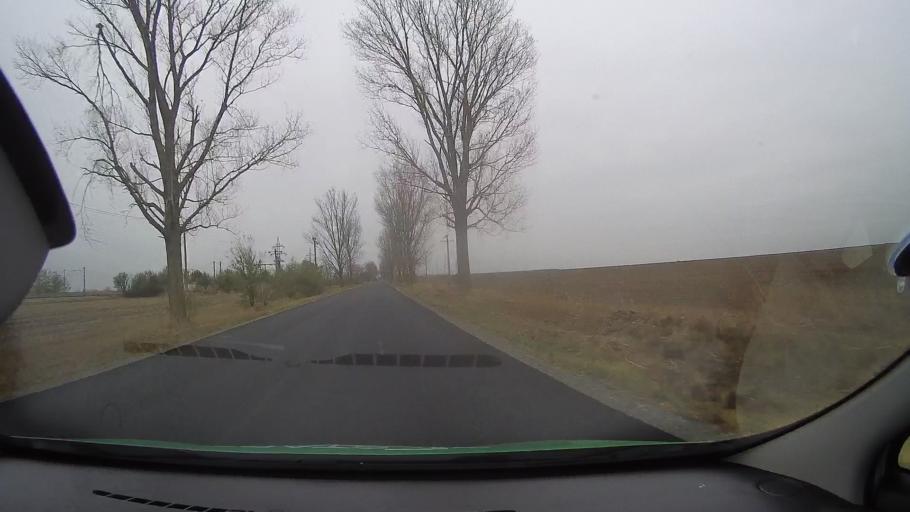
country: RO
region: Ialomita
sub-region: Comuna Valea Ciorii
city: Valea Ciorii
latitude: 44.7499
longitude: 27.5693
